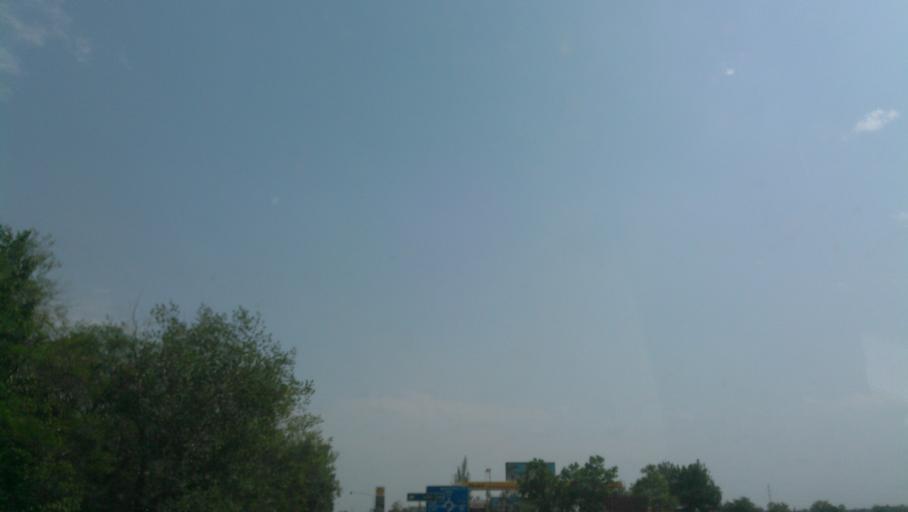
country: SK
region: Trnavsky
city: Samorin
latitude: 48.0845
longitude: 17.3827
